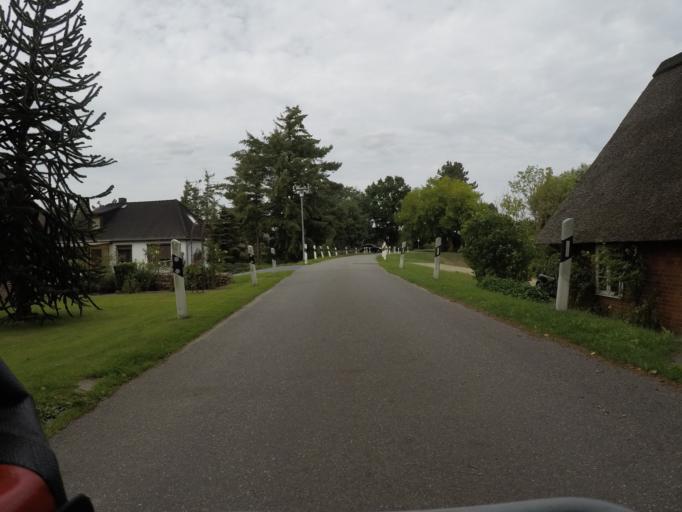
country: DE
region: Lower Saxony
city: Winsen
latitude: 53.3880
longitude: 10.1993
